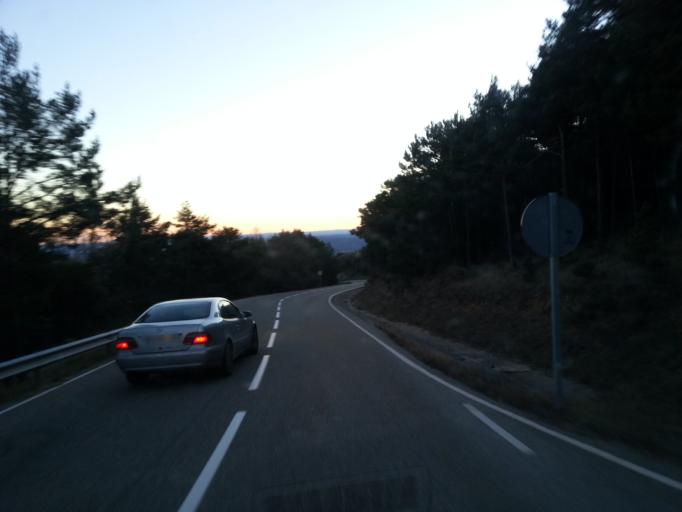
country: ES
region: Catalonia
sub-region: Provincia de Lleida
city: Olius
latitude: 42.0889
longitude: 1.5256
